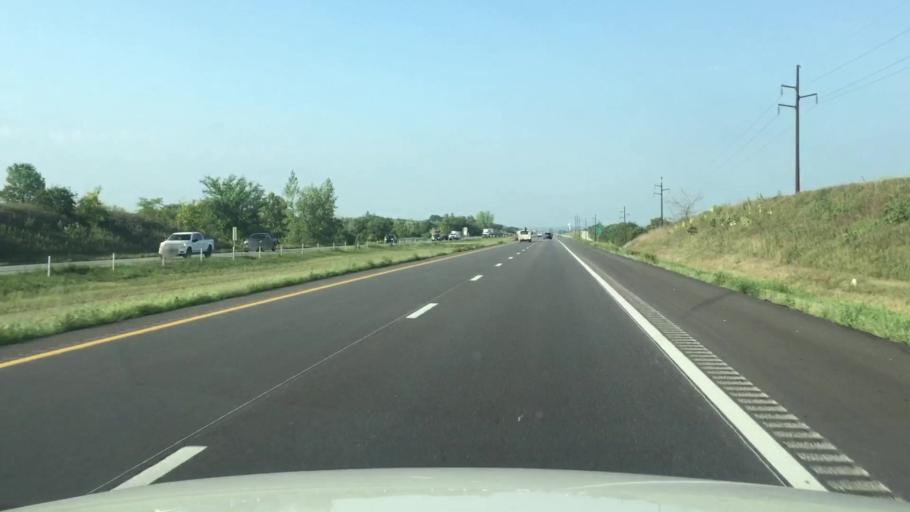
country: US
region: Missouri
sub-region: Clay County
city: Kearney
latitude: 39.3276
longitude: -94.3937
